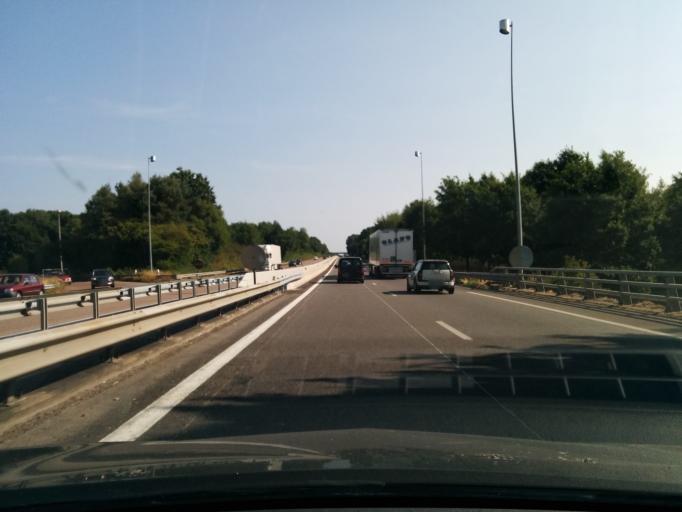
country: FR
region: Limousin
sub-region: Departement de la Haute-Vienne
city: Le Palais-sur-Vienne
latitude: 45.8735
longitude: 1.2878
